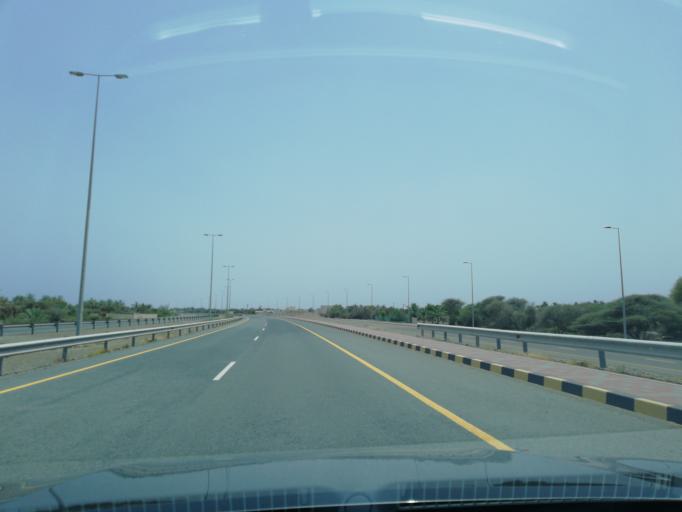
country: OM
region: Al Batinah
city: Shinas
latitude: 24.7960
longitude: 56.4518
